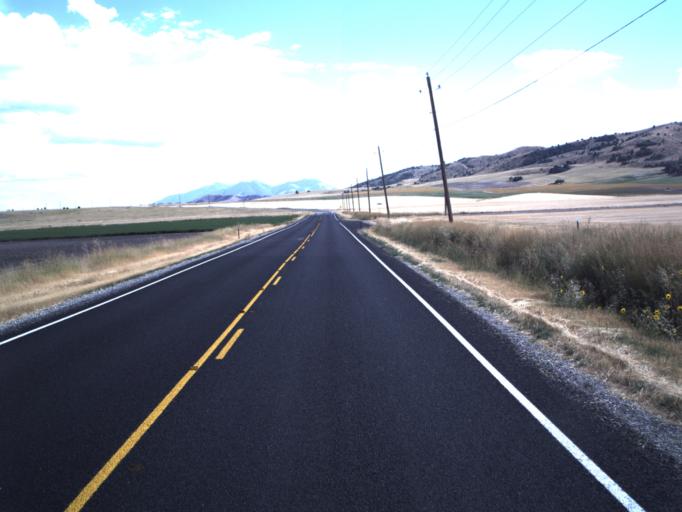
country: US
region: Utah
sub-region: Cache County
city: Benson
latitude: 41.9039
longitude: -112.0457
